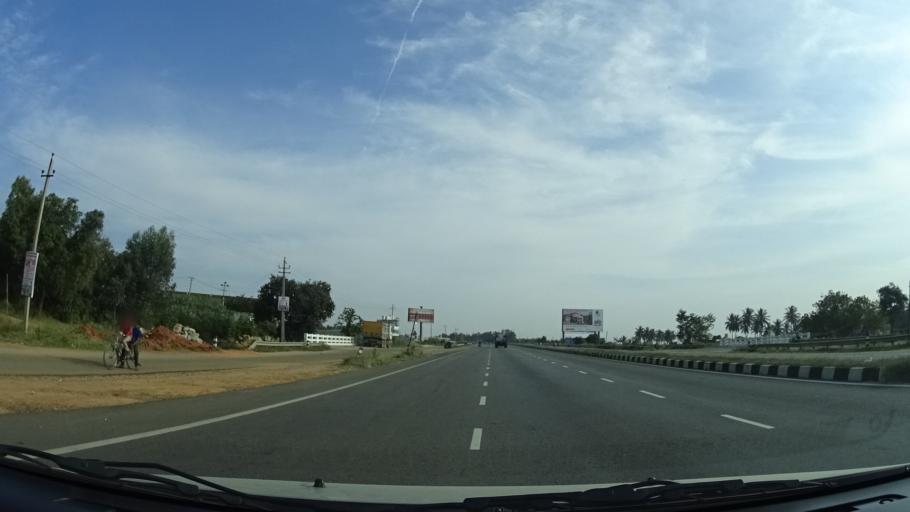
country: IN
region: Karnataka
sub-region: Bangalore Rural
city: Devanhalli
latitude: 13.2623
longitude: 77.7168
